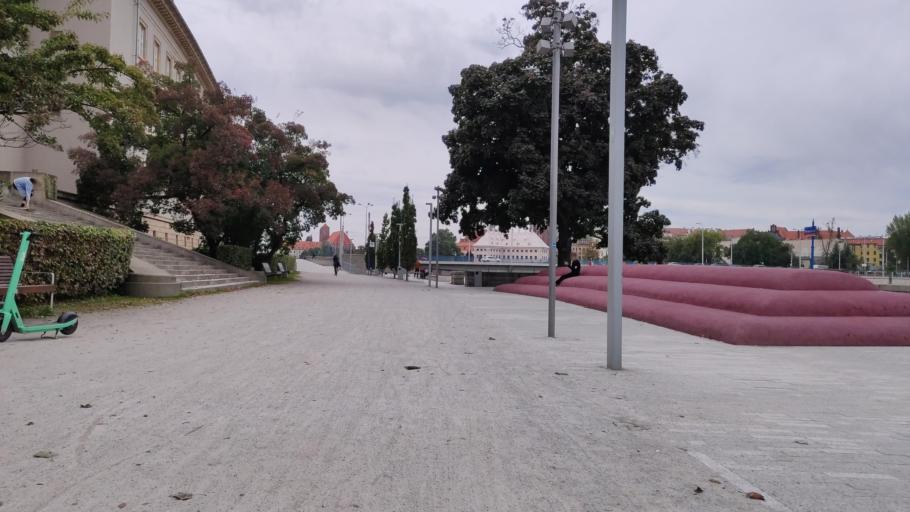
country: PL
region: Lower Silesian Voivodeship
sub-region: Powiat wroclawski
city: Wroclaw
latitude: 51.1103
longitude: 17.0504
